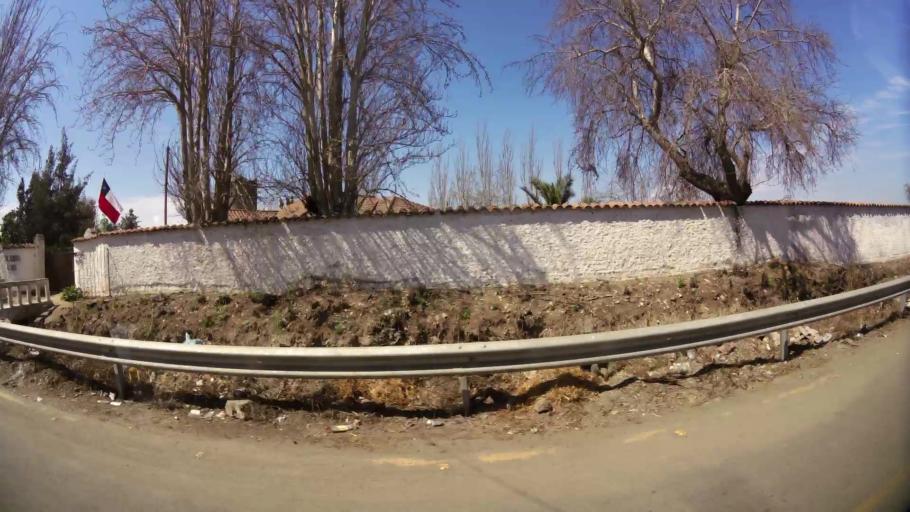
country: CL
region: Santiago Metropolitan
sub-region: Provincia de Talagante
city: Talagante
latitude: -33.6561
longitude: -70.9229
